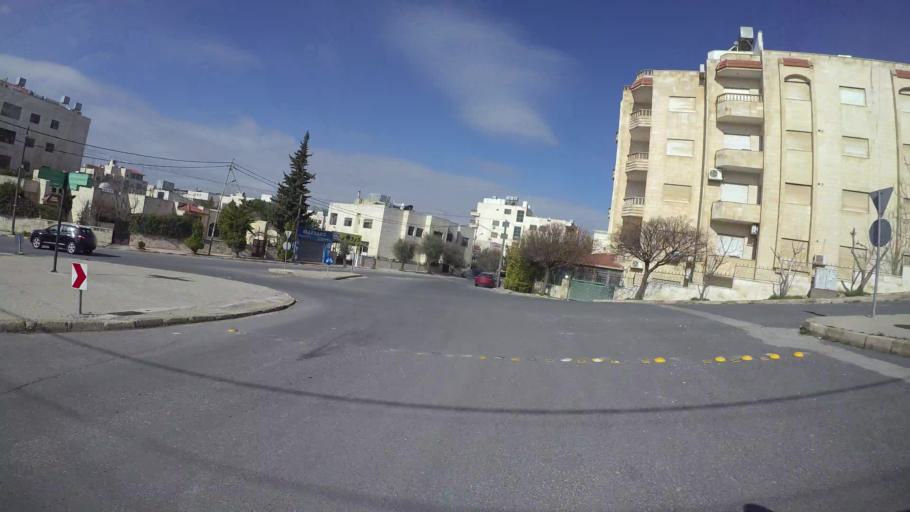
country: JO
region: Amman
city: Al Jubayhah
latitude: 32.0004
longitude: 35.8428
